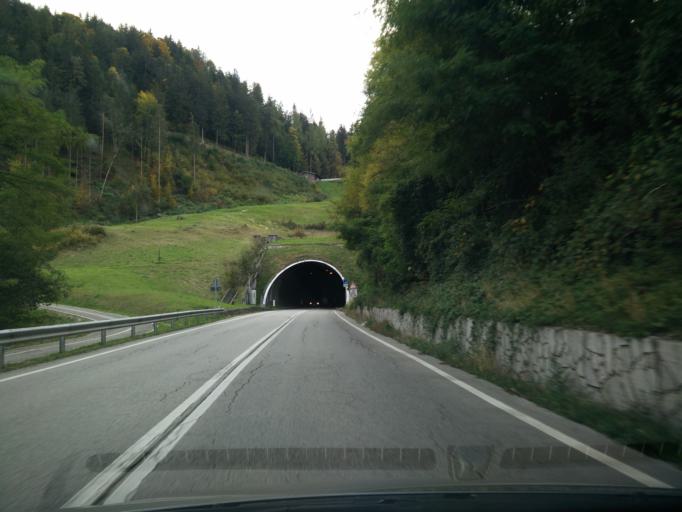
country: IT
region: Veneto
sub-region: Provincia di Belluno
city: Calalzo di Cadore
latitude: 46.4308
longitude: 12.3794
